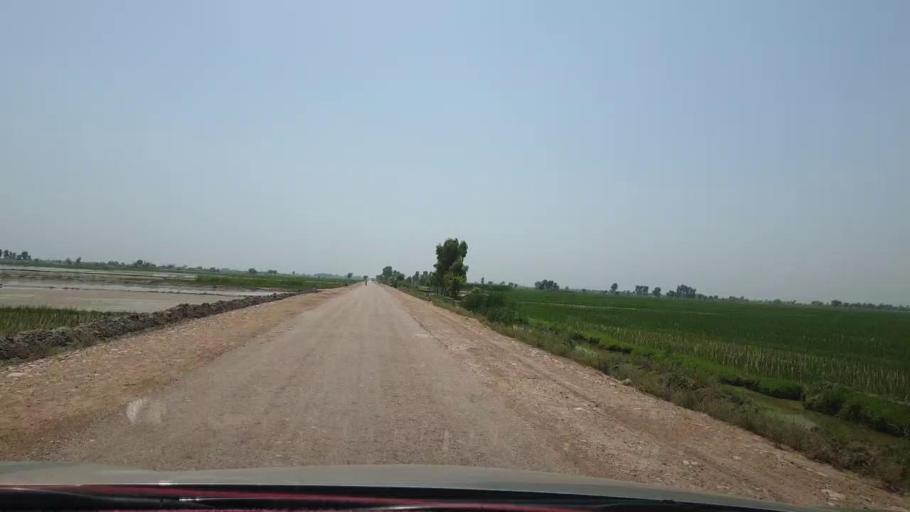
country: PK
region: Sindh
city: Warah
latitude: 27.5650
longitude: 67.8020
